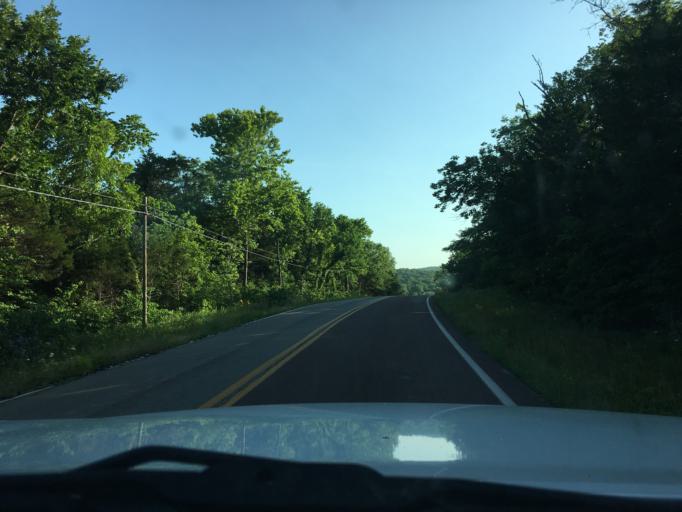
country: US
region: Missouri
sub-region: Gasconade County
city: Owensville
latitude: 38.4603
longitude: -91.6298
